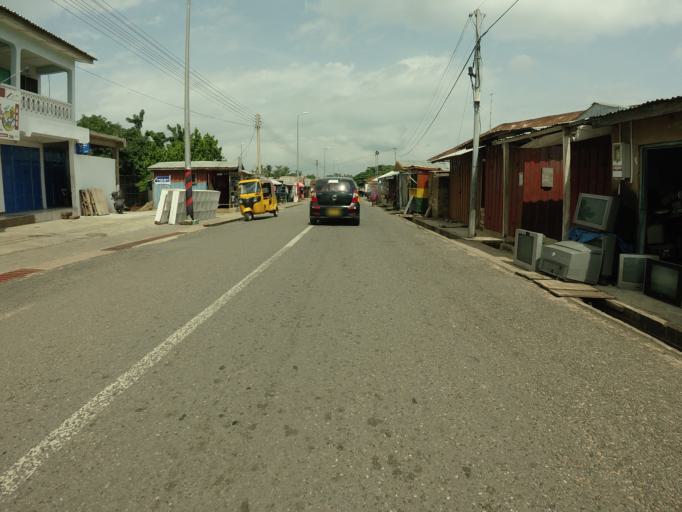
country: GH
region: Volta
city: Ho
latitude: 6.6158
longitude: 0.4700
